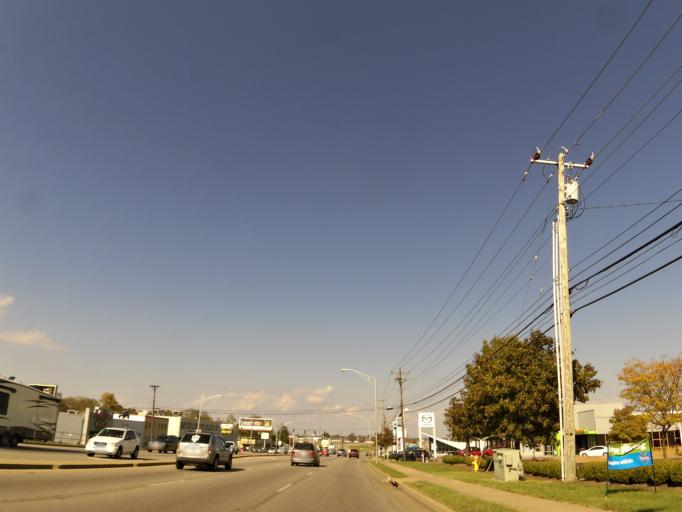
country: US
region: Kentucky
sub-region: Fayette County
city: Lexington-Fayette
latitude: 38.0368
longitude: -84.4542
